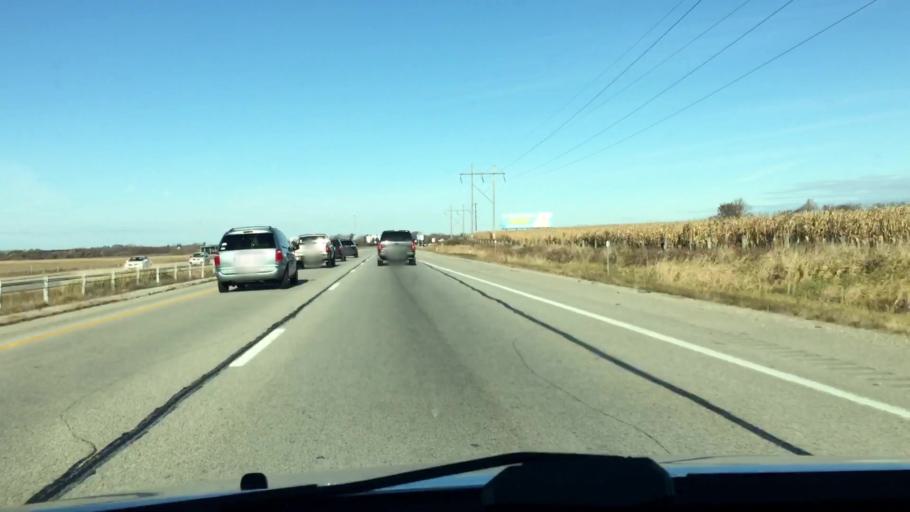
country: US
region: Wisconsin
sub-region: Fond du Lac County
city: North Fond du Lac
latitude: 43.8526
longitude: -88.5745
